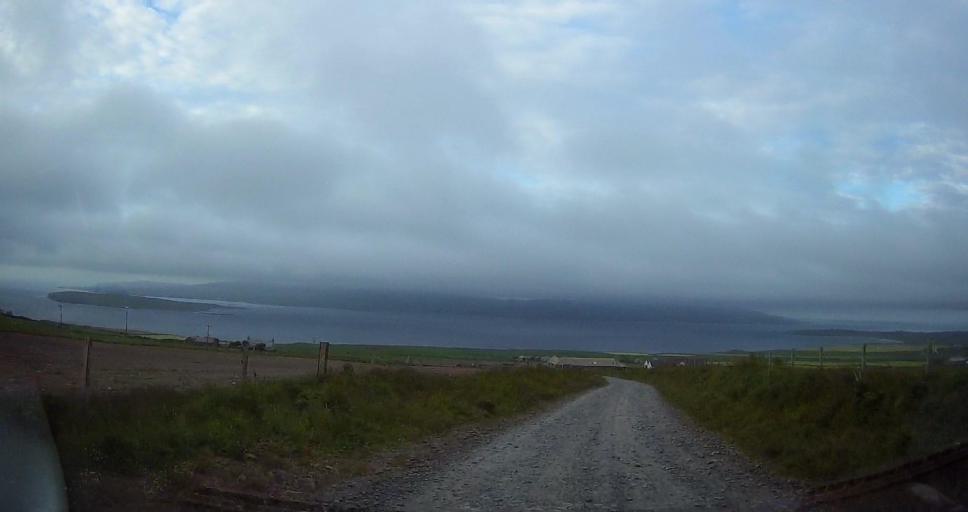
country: GB
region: Scotland
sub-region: Orkney Islands
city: Orkney
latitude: 59.1203
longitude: -3.1348
